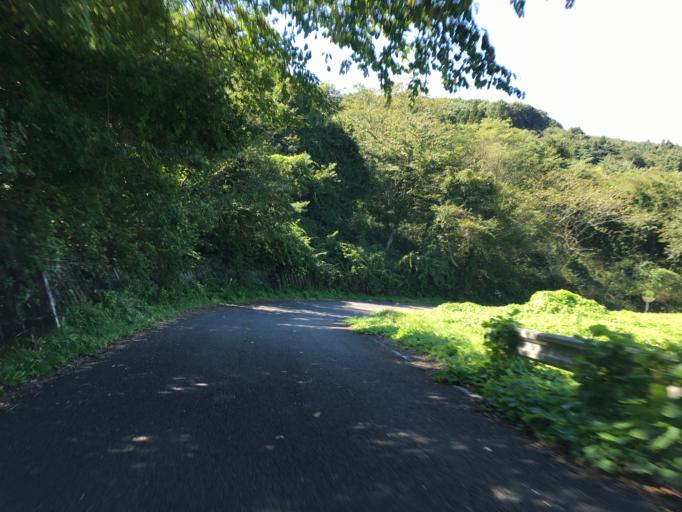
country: JP
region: Fukushima
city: Ishikawa
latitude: 37.2704
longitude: 140.5481
